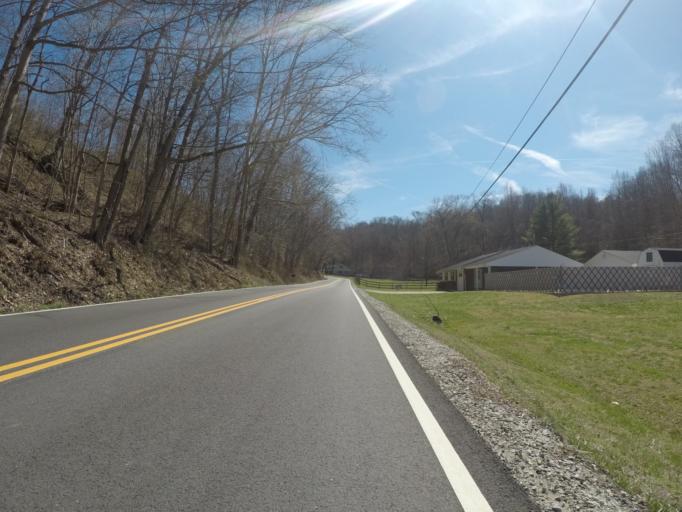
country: US
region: Ohio
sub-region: Lawrence County
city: South Point
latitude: 38.4635
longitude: -82.5601
